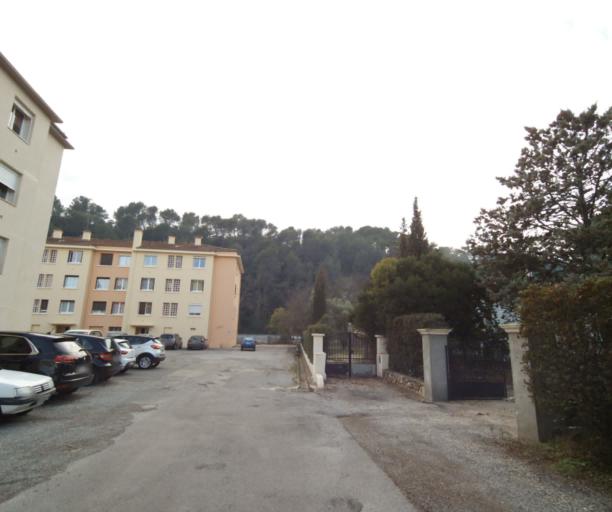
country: FR
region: Provence-Alpes-Cote d'Azur
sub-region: Departement du Var
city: Trans-en-Provence
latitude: 43.5067
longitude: 6.4808
